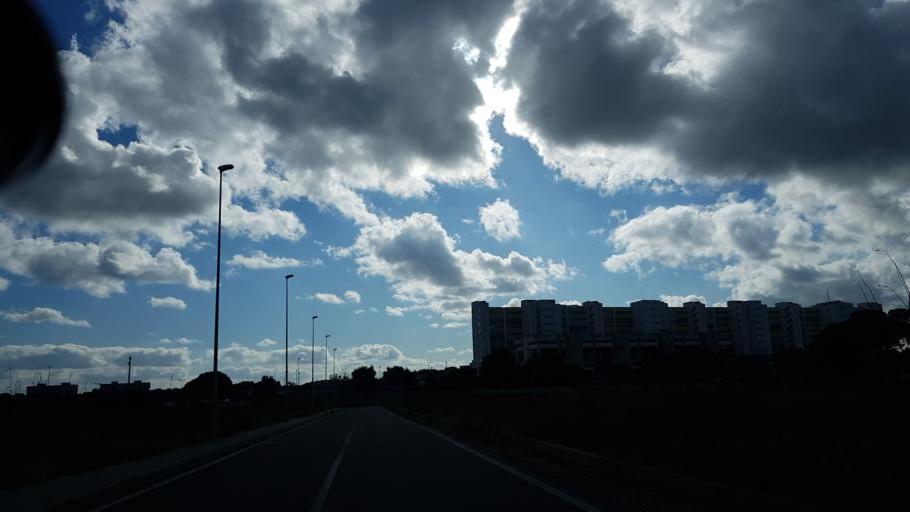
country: IT
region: Apulia
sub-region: Provincia di Brindisi
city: Brindisi
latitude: 40.6278
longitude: 17.9141
